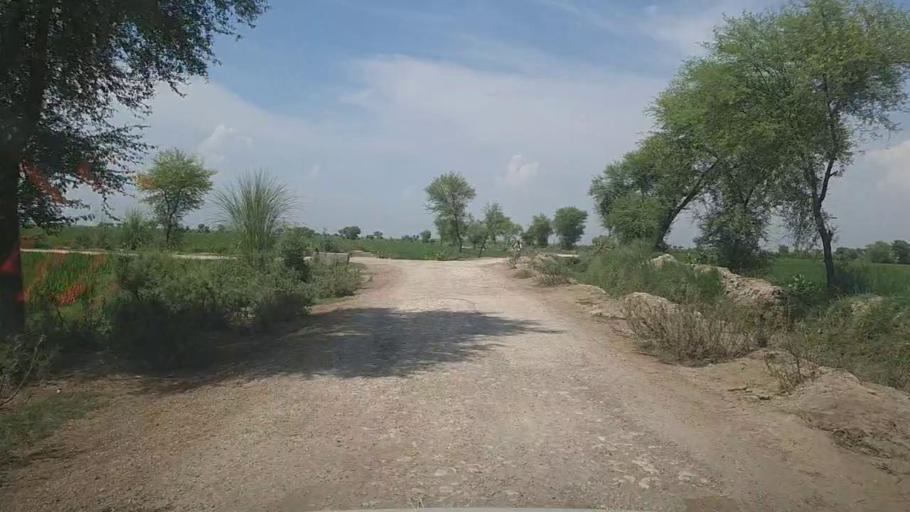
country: PK
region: Sindh
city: Kandhkot
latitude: 28.3058
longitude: 69.2428
